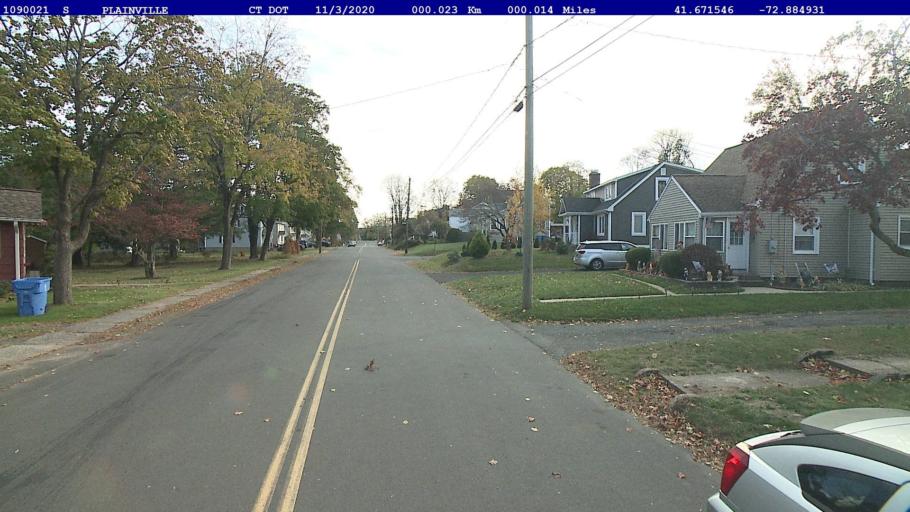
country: US
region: Connecticut
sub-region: Hartford County
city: Plainville
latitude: 41.6715
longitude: -72.8849
